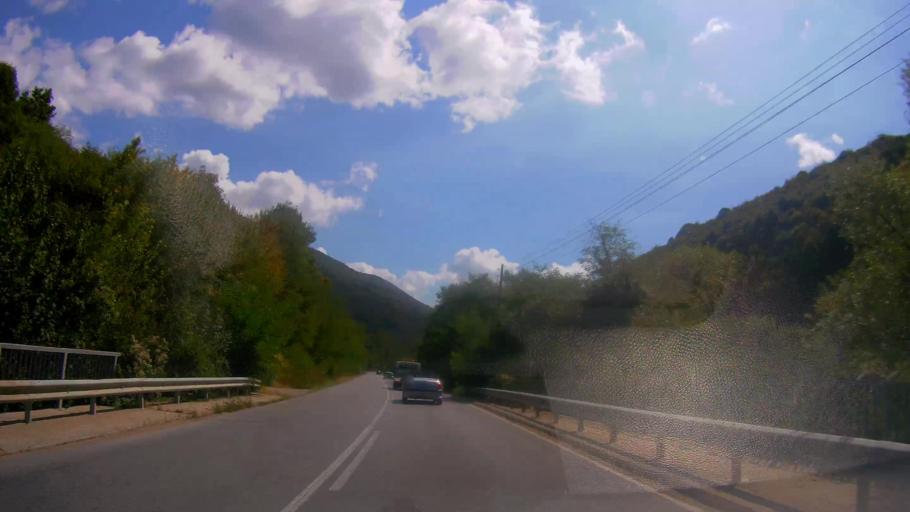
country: BG
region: Stara Zagora
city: Gurkovo
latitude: 42.7352
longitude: 25.7090
